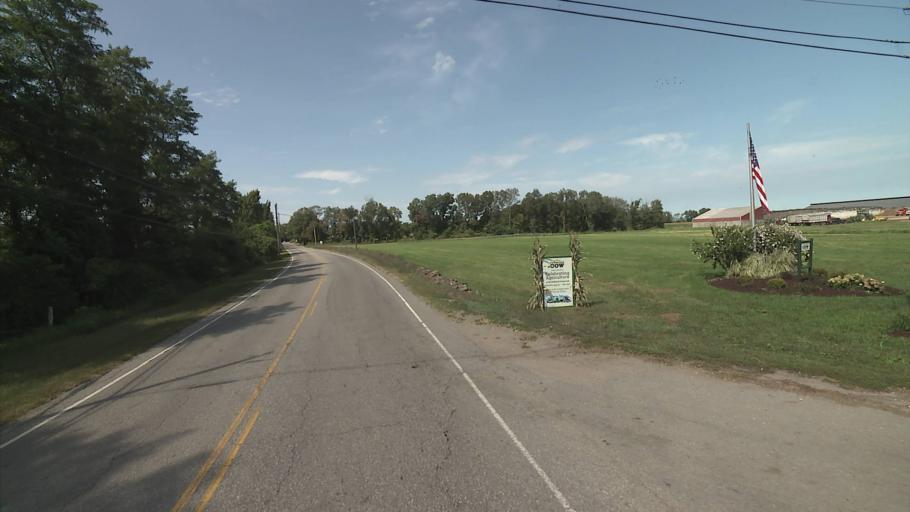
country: US
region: Connecticut
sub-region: Windham County
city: South Windham
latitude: 41.6044
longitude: -72.1694
